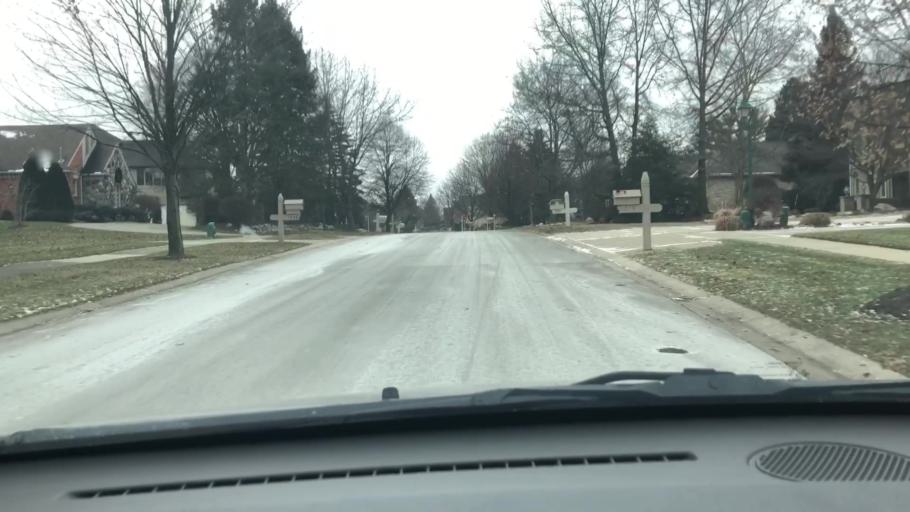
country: US
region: Michigan
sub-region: Oakland County
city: Rochester
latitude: 42.6904
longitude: -83.1132
